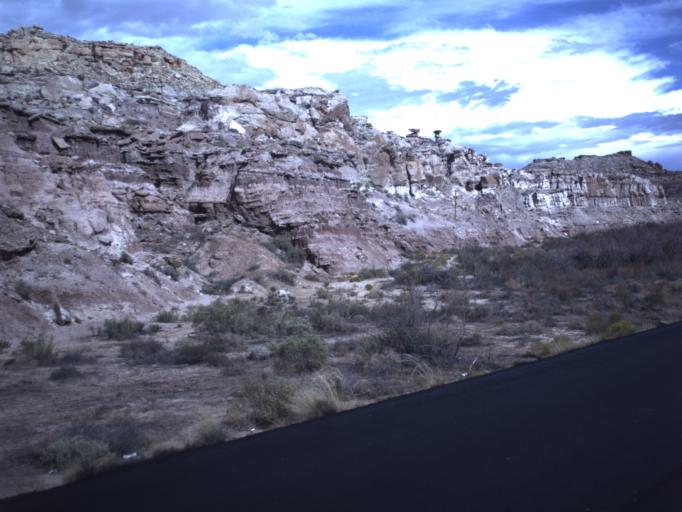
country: US
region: Utah
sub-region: San Juan County
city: Blanding
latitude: 37.2580
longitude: -109.2656
